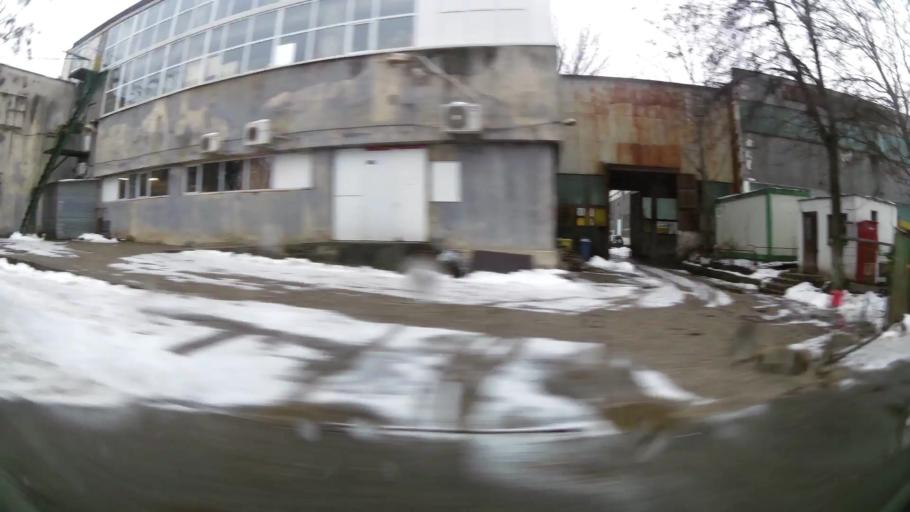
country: RO
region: Ilfov
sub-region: Comuna Otopeni
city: Otopeni
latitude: 44.4857
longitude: 26.0669
